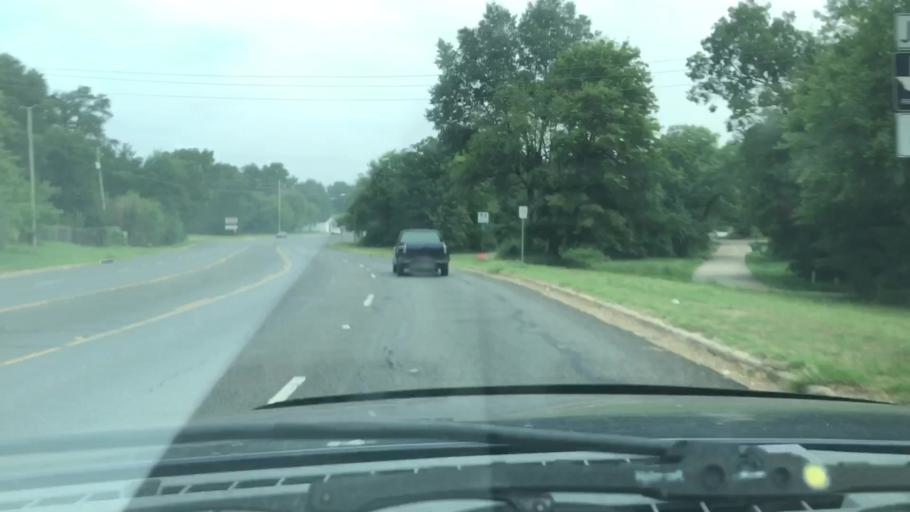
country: US
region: Texas
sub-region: Bowie County
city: Texarkana
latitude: 33.4377
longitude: -94.0629
